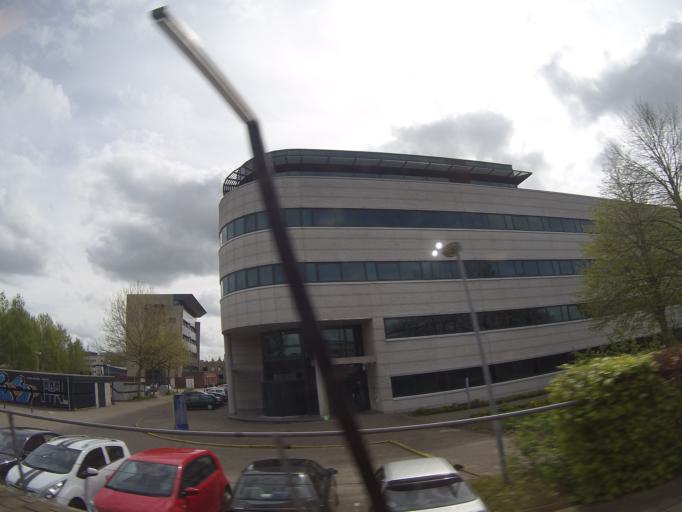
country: NL
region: Utrecht
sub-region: Gemeente Amersfoort
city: Randenbroek
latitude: 52.1758
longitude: 5.4057
